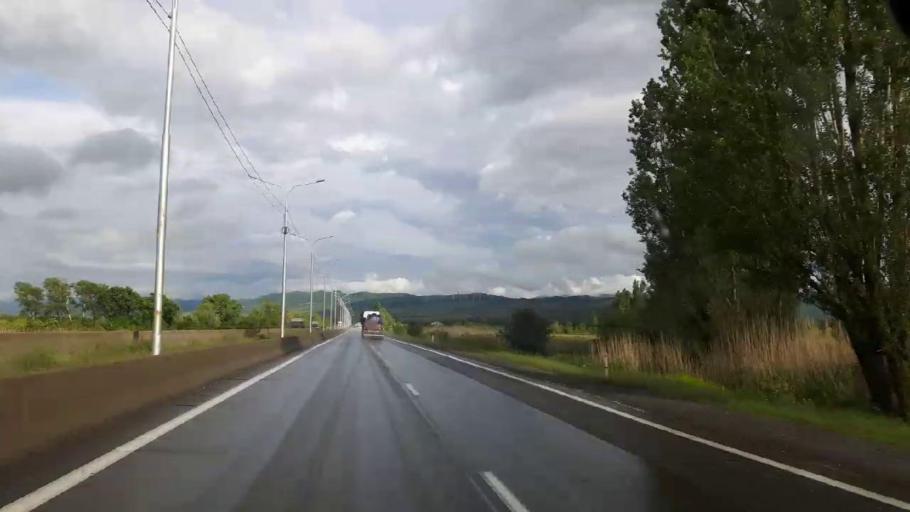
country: GE
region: Shida Kartli
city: Kaspi
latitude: 41.9233
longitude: 44.5426
